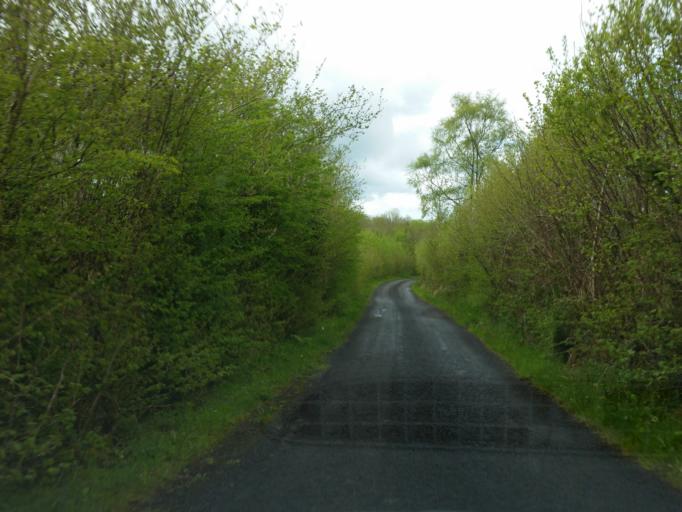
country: GB
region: Northern Ireland
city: Lisnaskea
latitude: 54.2633
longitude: -7.3953
